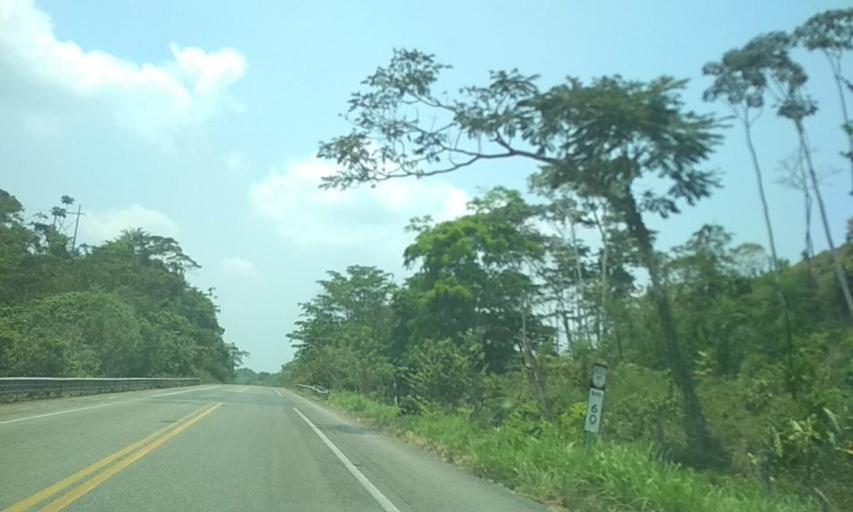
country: MX
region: Tabasco
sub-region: Huimanguillo
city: Francisco Rueda
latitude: 17.6808
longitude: -93.8866
